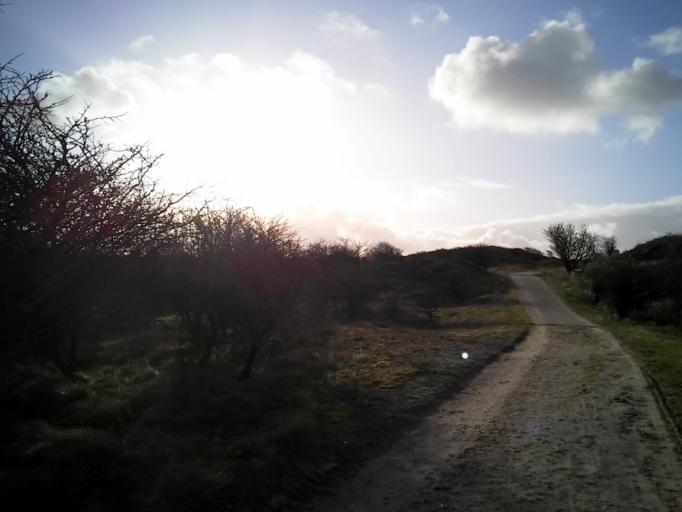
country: NL
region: South Holland
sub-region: Gemeente Noordwijkerhout
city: Noordwijkerhout
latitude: 52.2999
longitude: 4.4952
